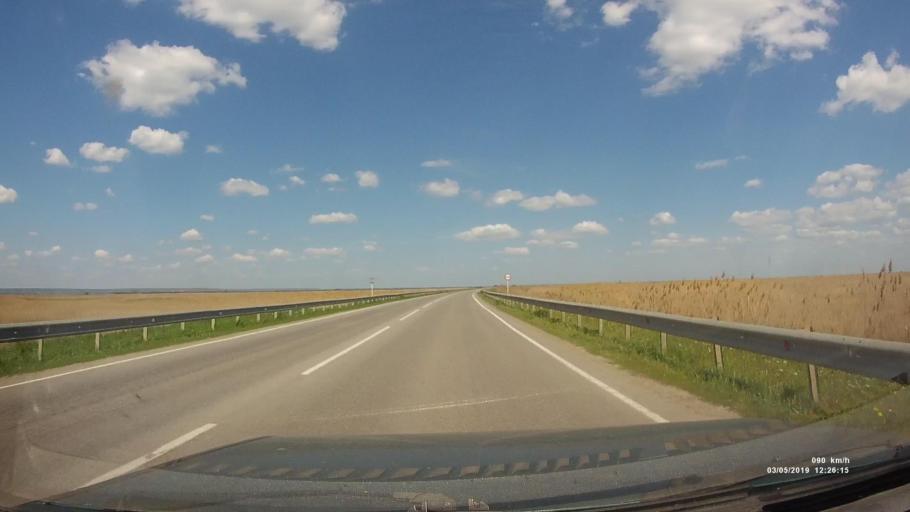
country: RU
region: Rostov
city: Semikarakorsk
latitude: 47.4426
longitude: 40.7125
